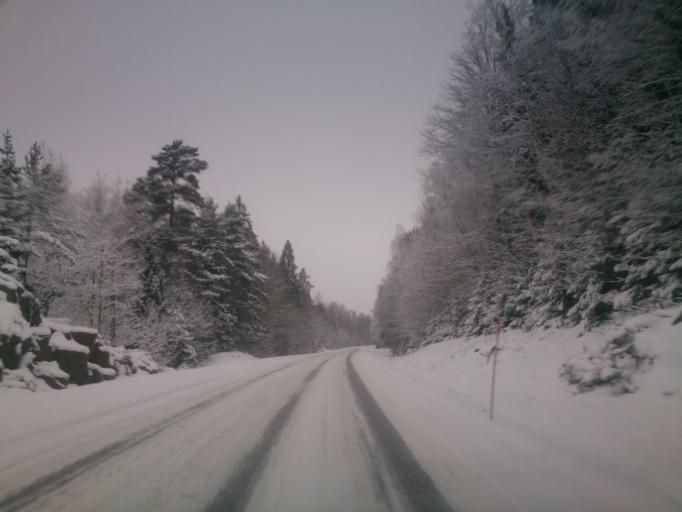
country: SE
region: OEstergoetland
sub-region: Norrkopings Kommun
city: Skarblacka
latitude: 58.6134
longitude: 15.8111
